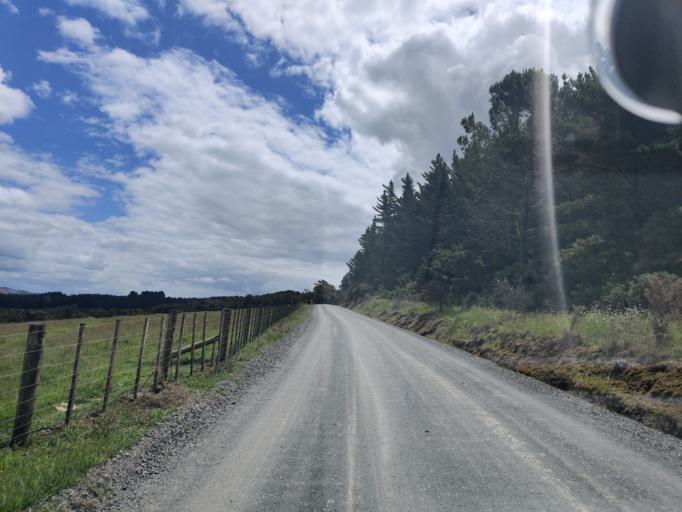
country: NZ
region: Northland
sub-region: Far North District
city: Paihia
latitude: -35.2593
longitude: 174.0648
